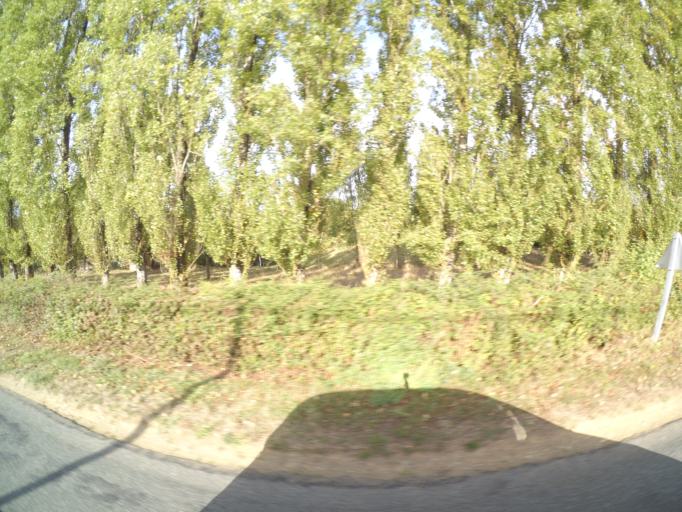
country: FR
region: Pays de la Loire
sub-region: Departement de Maine-et-Loire
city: Saint-Crespin-sur-Moine
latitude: 47.1296
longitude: -1.1970
